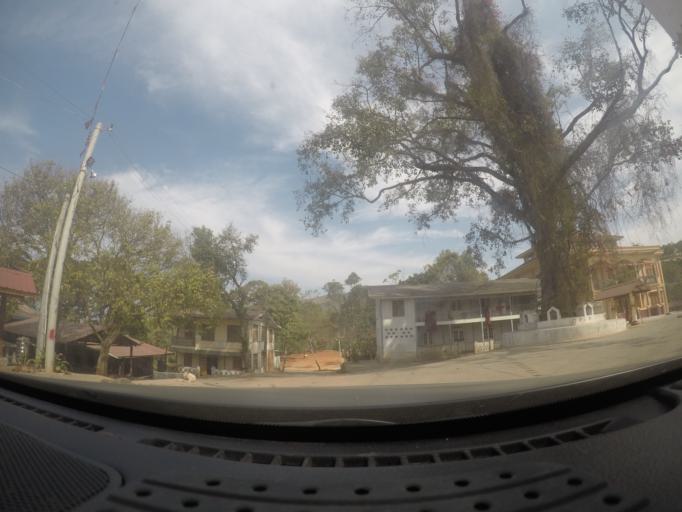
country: MM
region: Mandalay
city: Yamethin
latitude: 20.6387
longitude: 96.5663
